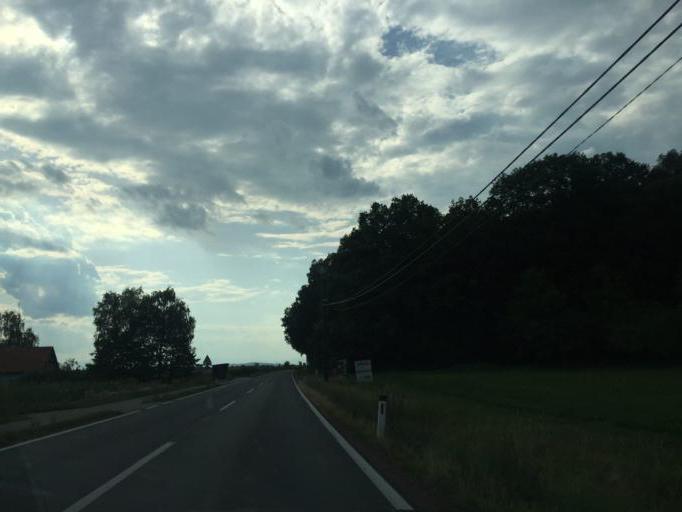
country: AT
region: Styria
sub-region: Politischer Bezirk Suedoststeiermark
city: Weinburg am Sassbach
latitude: 46.7547
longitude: 15.6898
